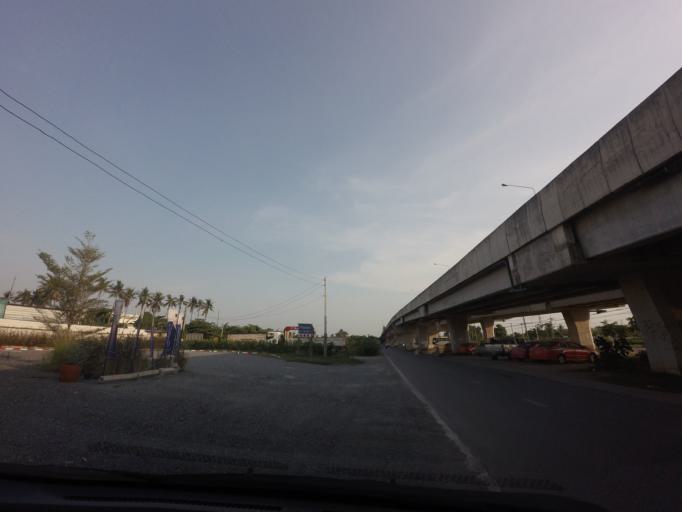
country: TH
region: Bangkok
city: Taling Chan
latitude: 13.7551
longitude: 100.4274
